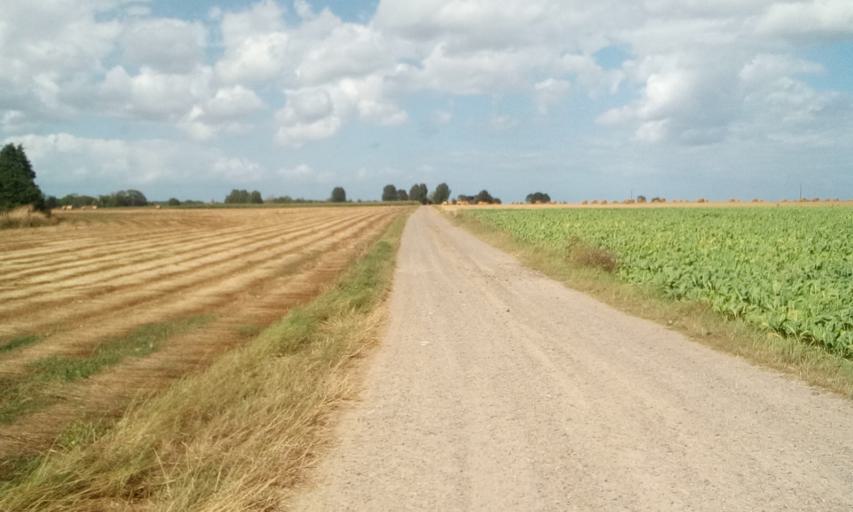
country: FR
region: Lower Normandy
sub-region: Departement du Calvados
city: Ver-sur-Mer
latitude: 49.3225
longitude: -0.5280
